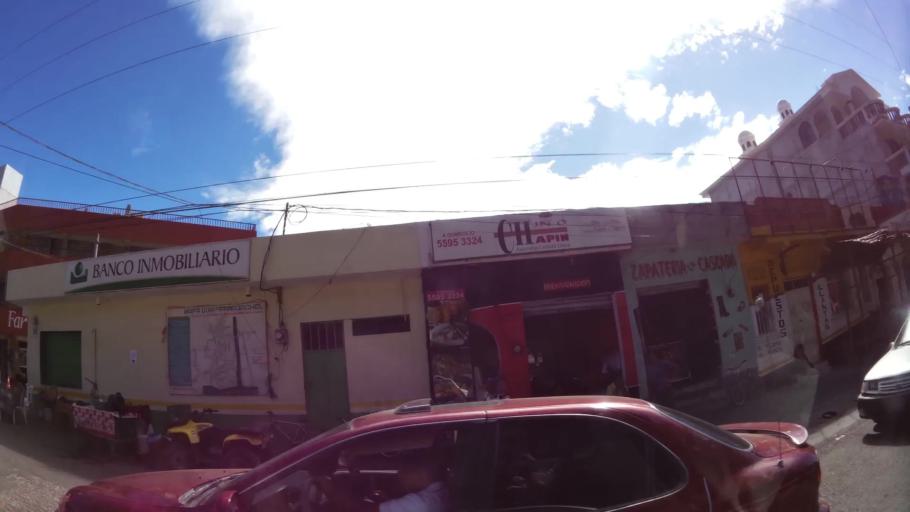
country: GT
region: Solola
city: Panajachel
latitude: 14.7440
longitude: -91.1563
